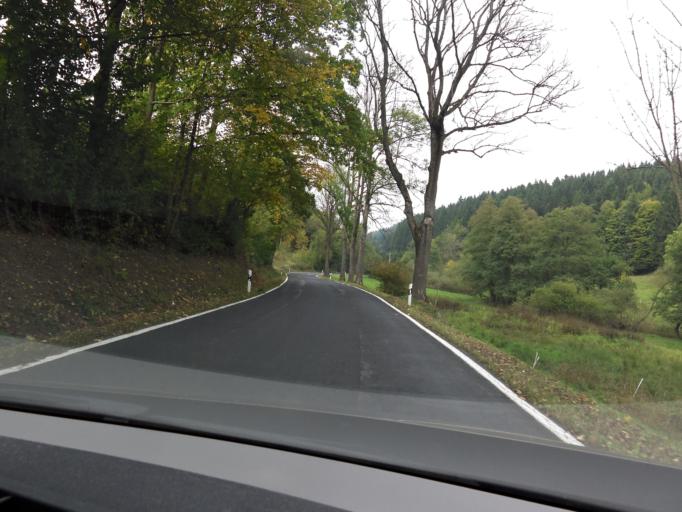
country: DE
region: Thuringia
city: Pappenheim
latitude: 50.8051
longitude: 10.4715
